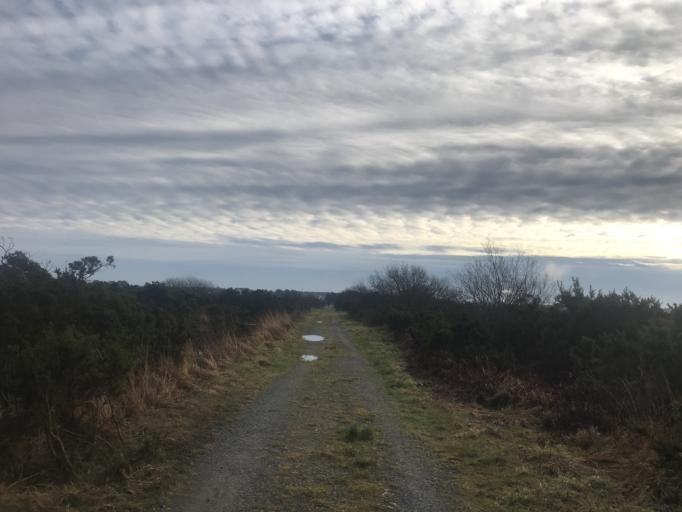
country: IE
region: Connaught
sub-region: County Galway
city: Gaillimh
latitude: 53.3215
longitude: -9.0106
